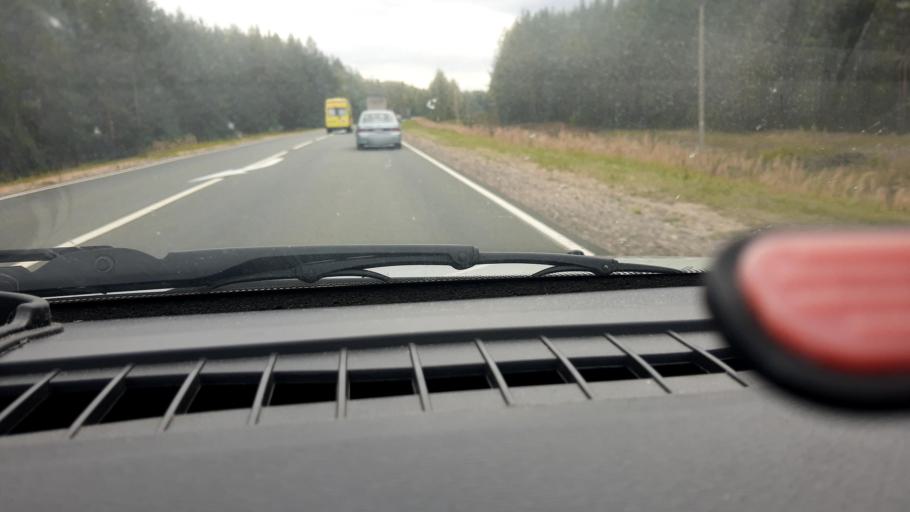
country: RU
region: Nizjnij Novgorod
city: Uren'
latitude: 57.3958
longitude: 45.6871
